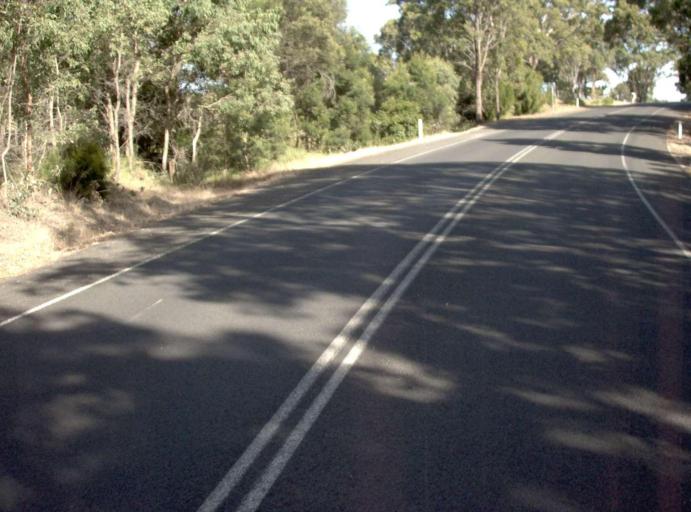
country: AU
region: Victoria
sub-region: East Gippsland
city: Lakes Entrance
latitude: -37.8756
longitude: 147.8496
